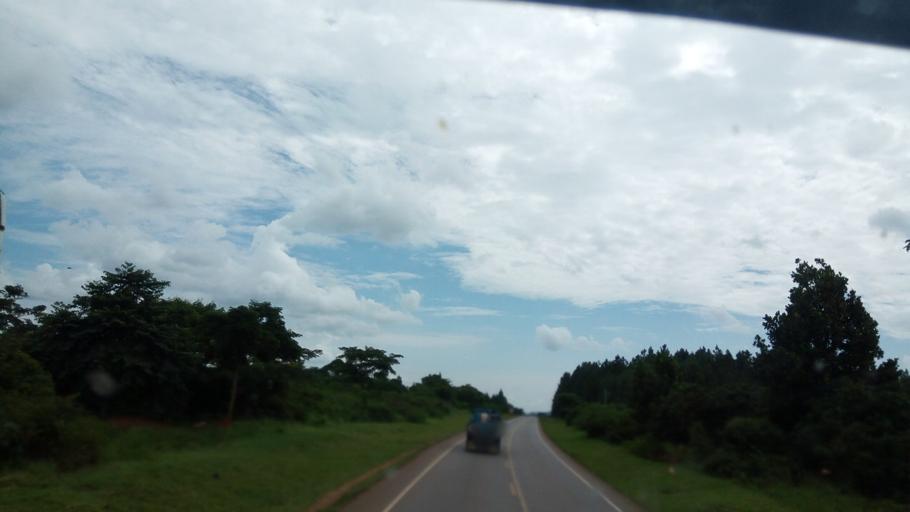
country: UG
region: Central Region
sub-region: Nakasongola District
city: Nakasongola
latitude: 1.1879
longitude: 32.4607
